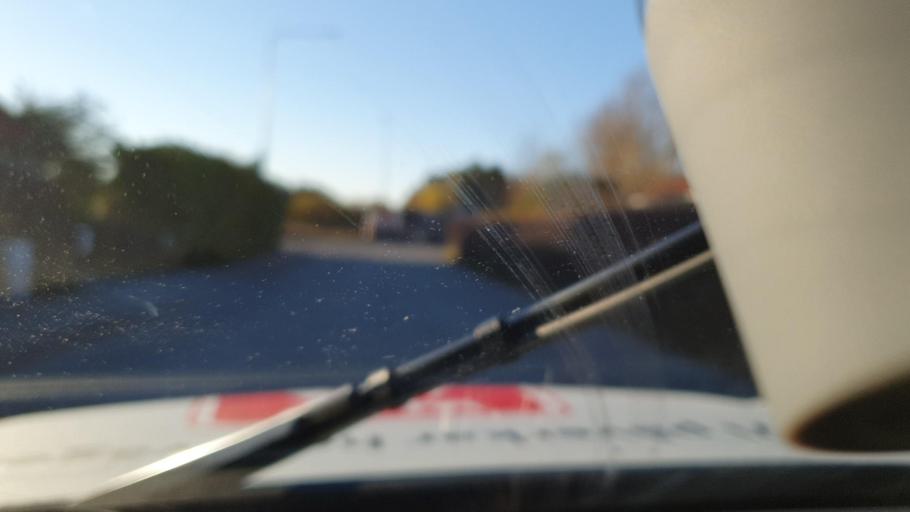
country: SE
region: Stockholm
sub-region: Vallentuna Kommun
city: Vallentuna
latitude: 59.4977
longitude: 18.0824
